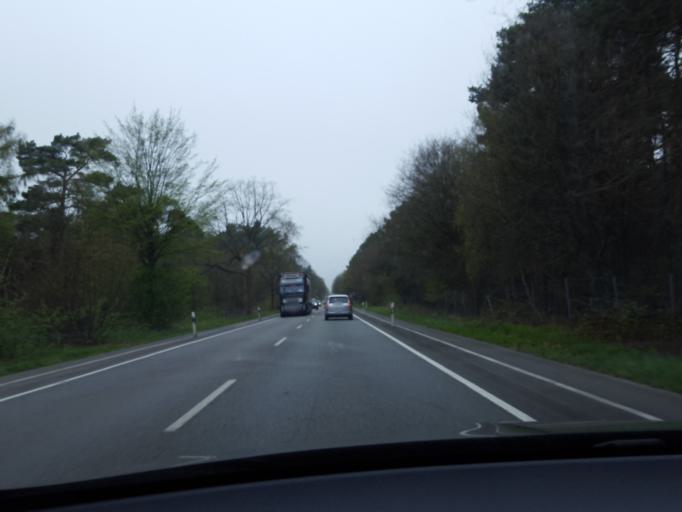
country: DE
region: North Rhine-Westphalia
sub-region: Regierungsbezirk Munster
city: Raesfeld
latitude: 51.7355
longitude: 6.8907
